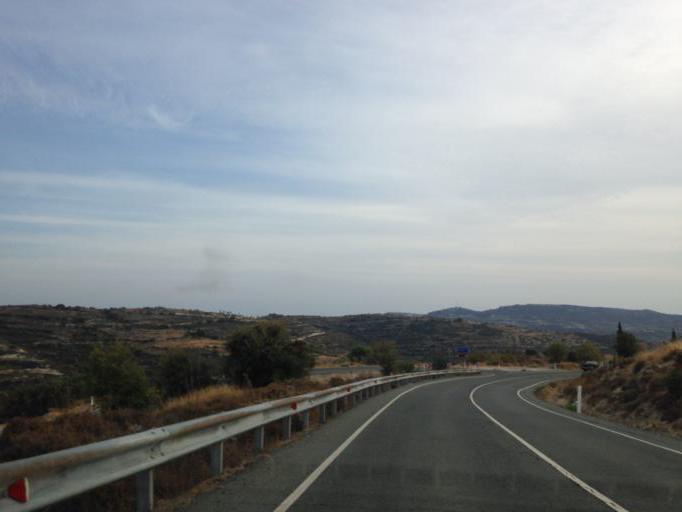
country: CY
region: Limassol
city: Pachna
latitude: 34.8196
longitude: 32.7976
